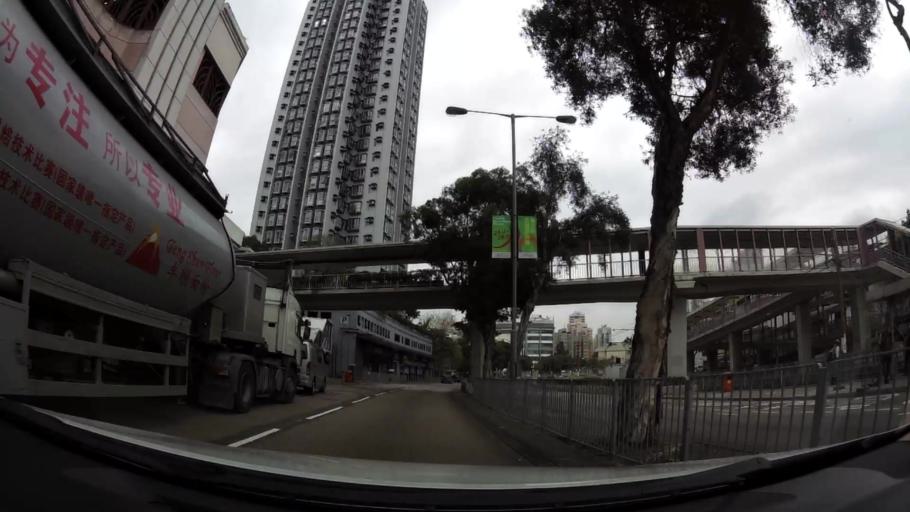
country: HK
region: Tuen Mun
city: Tuen Mun
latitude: 22.3978
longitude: 113.9772
